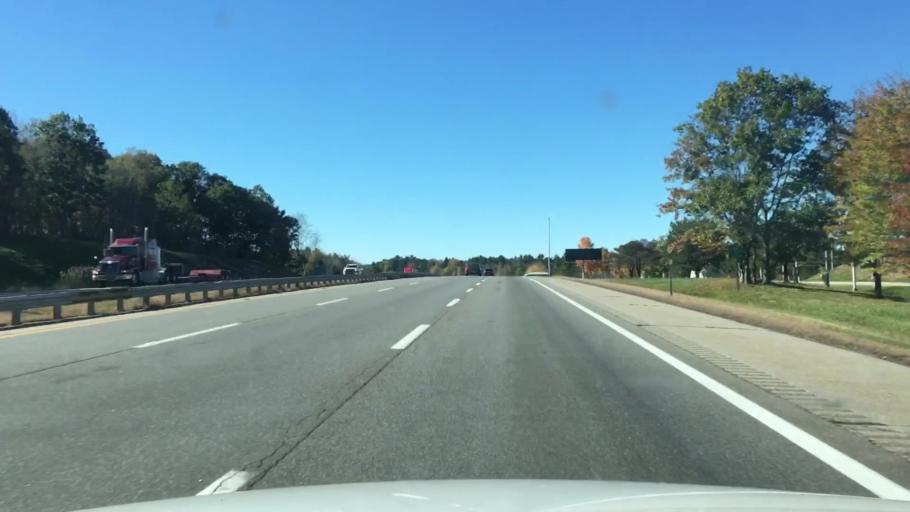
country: US
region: Maine
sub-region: York County
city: Kittery Point
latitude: 43.1363
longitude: -70.7080
